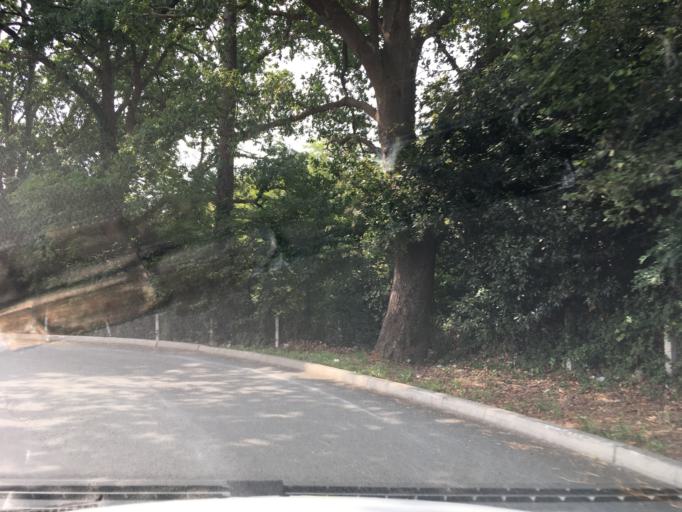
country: FR
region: Aquitaine
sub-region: Departement des Pyrenees-Atlantiques
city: Anglet
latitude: 43.4737
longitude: -1.5323
